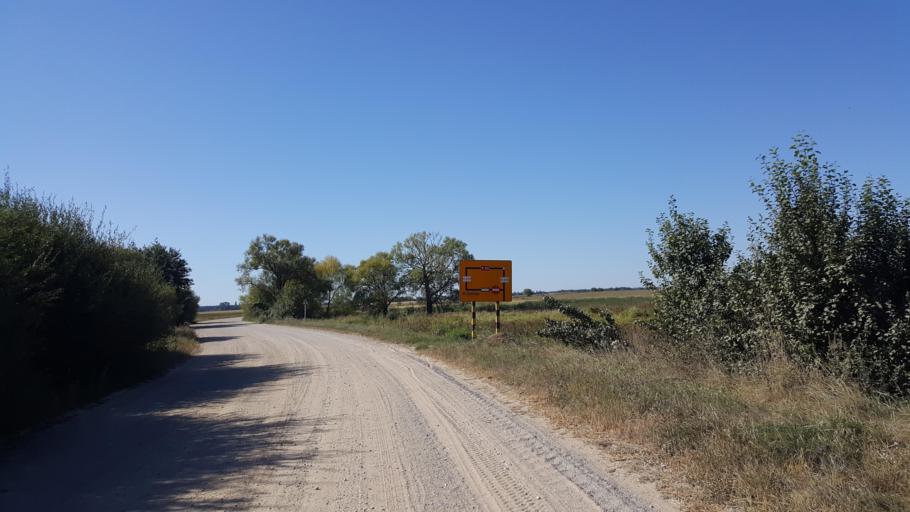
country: BY
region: Brest
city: Charnawchytsy
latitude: 52.3387
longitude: 23.6360
